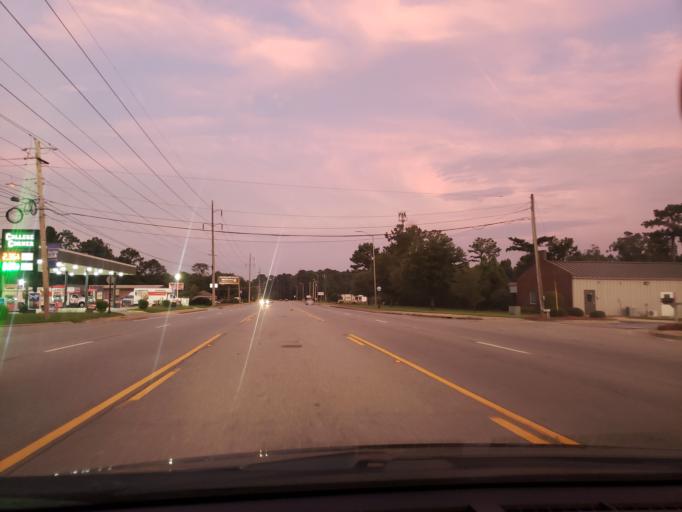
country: US
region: Georgia
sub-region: Dougherty County
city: Albany
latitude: 31.5845
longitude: -84.2051
